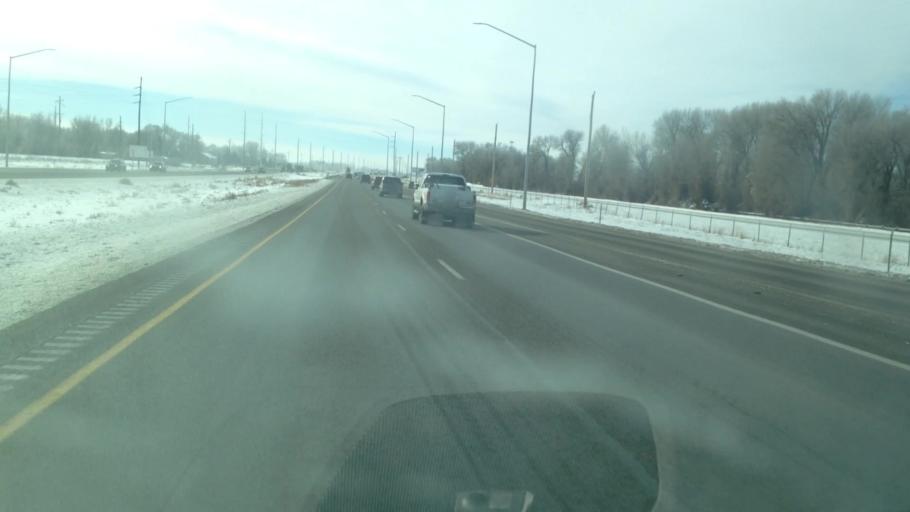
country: US
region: Idaho
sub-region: Madison County
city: Rexburg
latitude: 43.7580
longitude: -111.8468
